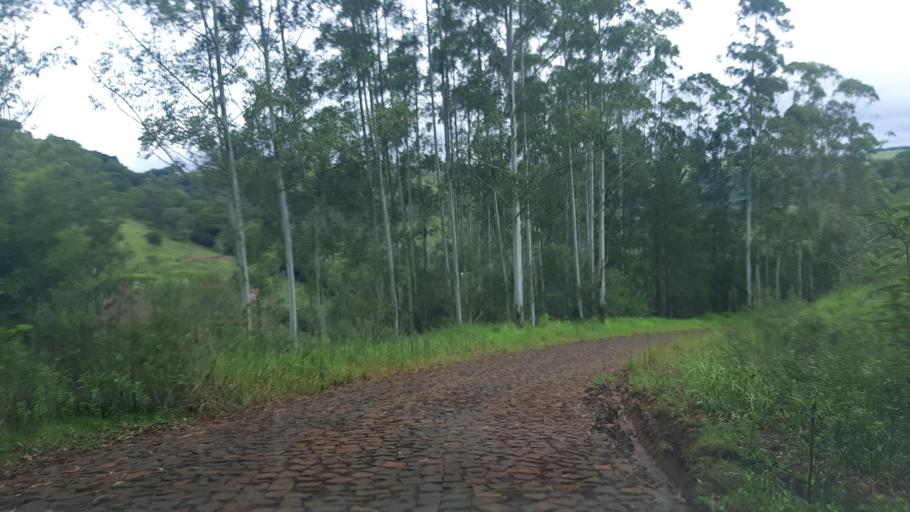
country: BR
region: Parana
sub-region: Ampere
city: Ampere
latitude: -26.0412
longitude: -53.5135
